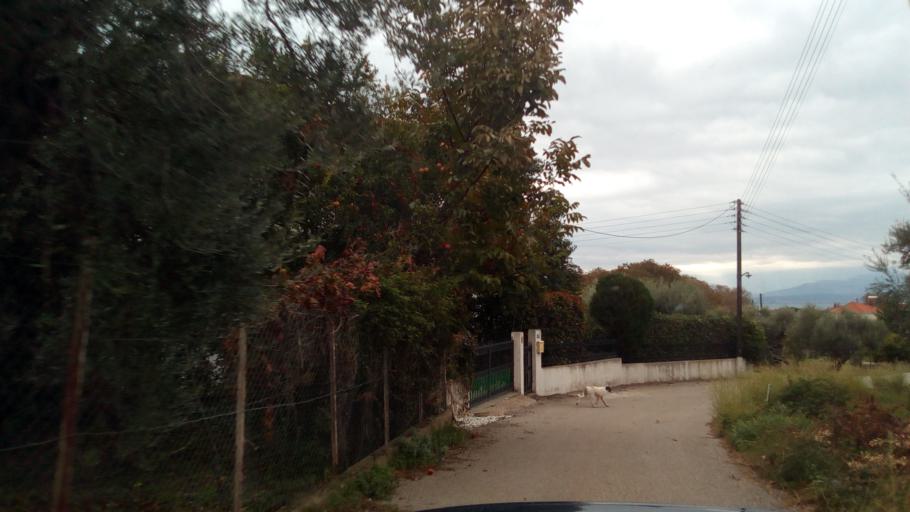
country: GR
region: West Greece
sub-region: Nomos Achaias
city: Kamarai
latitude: 38.3936
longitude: 22.0583
